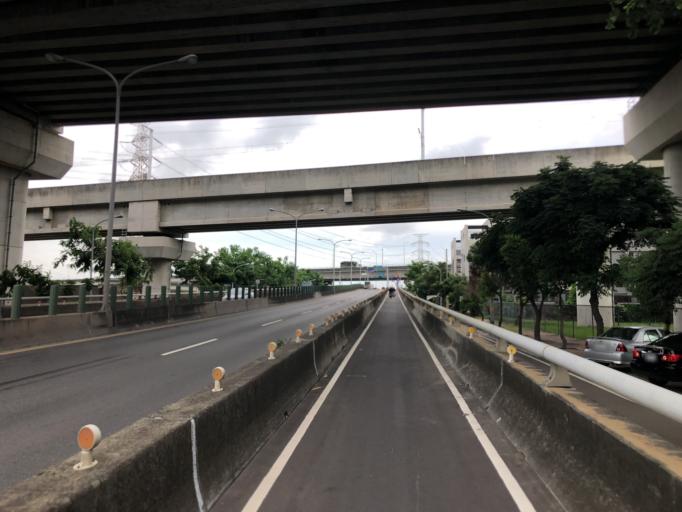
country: TW
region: Taiwan
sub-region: Changhua
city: Chang-hua
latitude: 24.1029
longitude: 120.6155
